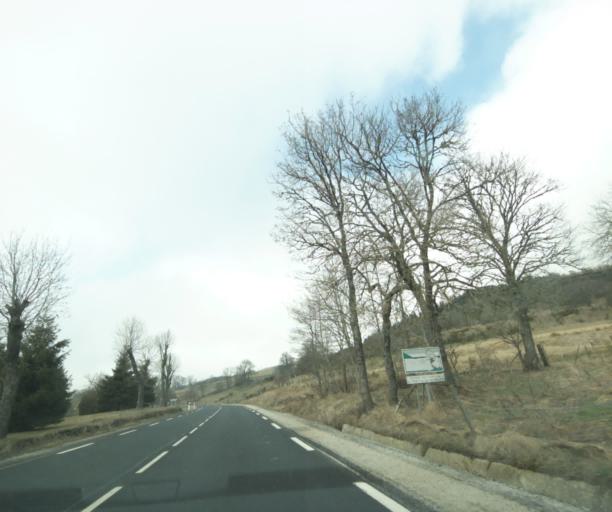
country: FR
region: Languedoc-Roussillon
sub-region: Departement de la Lozere
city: Langogne
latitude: 44.7586
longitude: 3.8904
